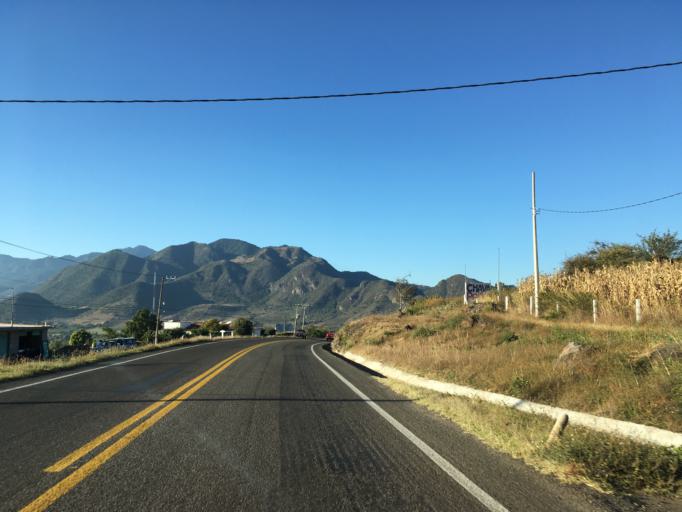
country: MX
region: Michoacan
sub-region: Tuxpan
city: La Soledad
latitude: 19.5313
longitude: -100.4751
